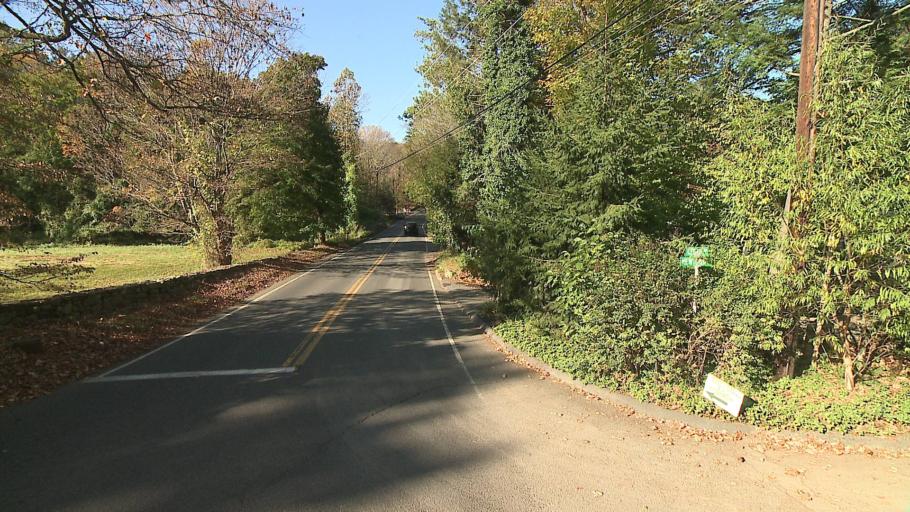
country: US
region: Connecticut
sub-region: Fairfield County
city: Wilton
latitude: 41.1993
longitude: -73.3892
